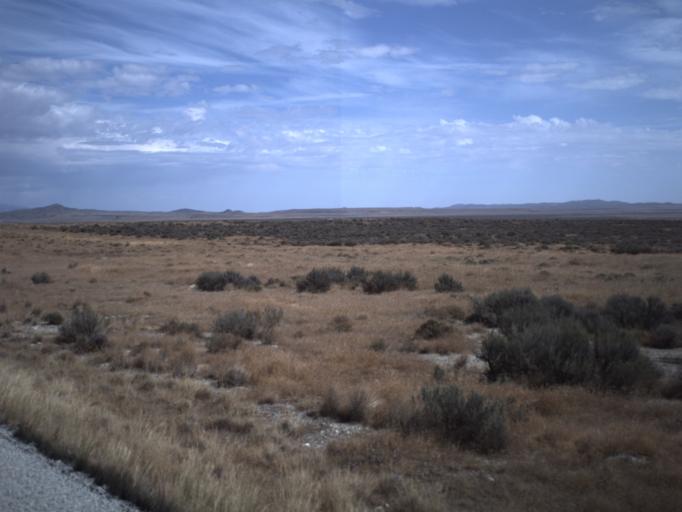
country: US
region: Utah
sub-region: Tooele County
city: Wendover
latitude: 41.5469
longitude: -113.5881
